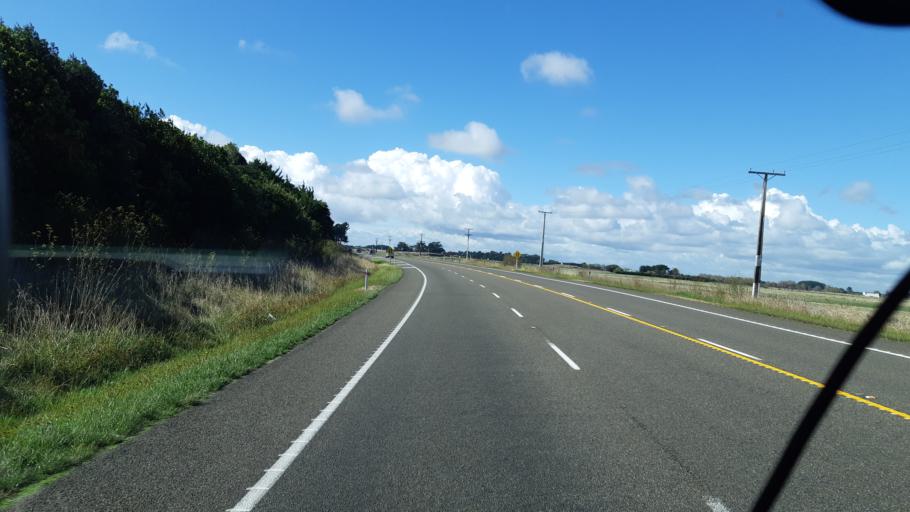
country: NZ
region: Manawatu-Wanganui
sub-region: Wanganui District
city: Wanganui
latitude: -39.9751
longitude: 175.1205
